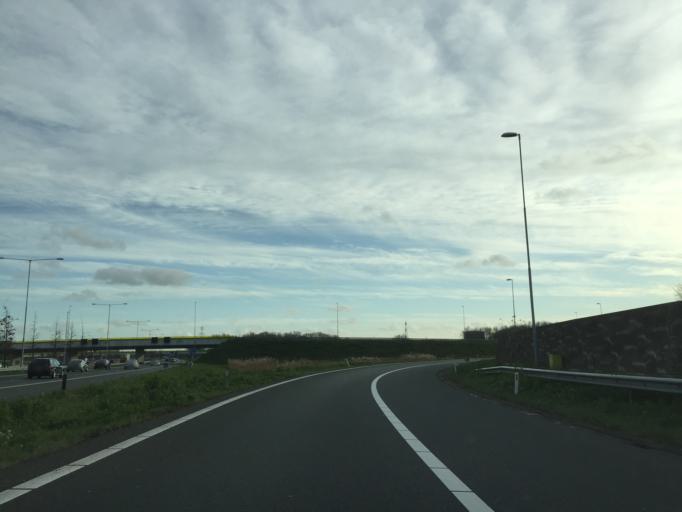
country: NL
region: North Brabant
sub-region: Gemeente 's-Hertogenbosch
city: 's-Hertogenbosch
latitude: 51.7258
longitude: 5.3206
